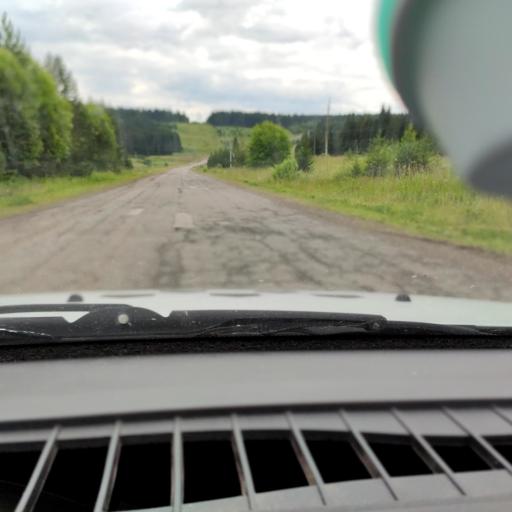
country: RU
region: Perm
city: Uinskoye
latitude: 57.1211
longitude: 56.5526
